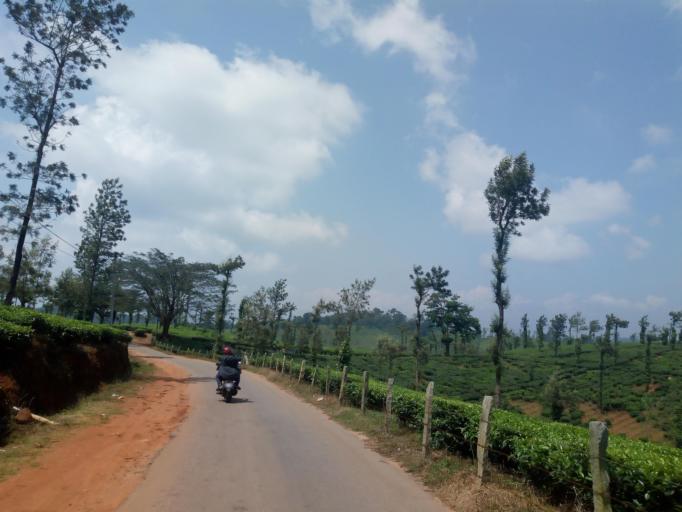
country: IN
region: Karnataka
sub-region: Kodagu
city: Ponnampet
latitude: 12.0316
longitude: 75.9417
